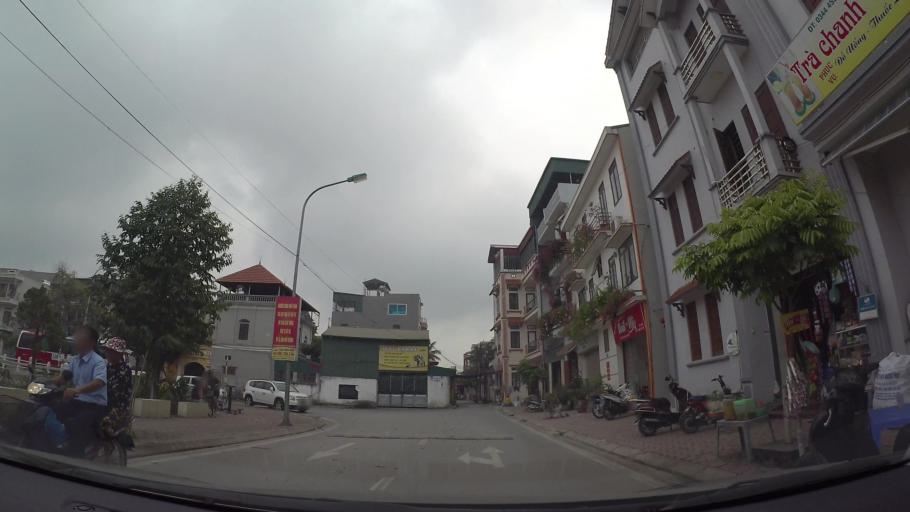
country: VN
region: Ha Noi
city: Trau Quy
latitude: 21.0403
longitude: 105.9291
